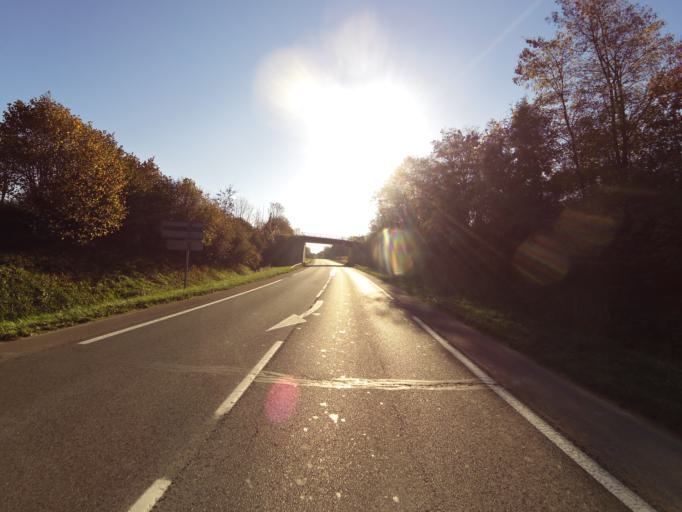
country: FR
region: Champagne-Ardenne
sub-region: Departement de l'Aube
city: Breviandes
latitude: 48.2587
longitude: 4.0980
